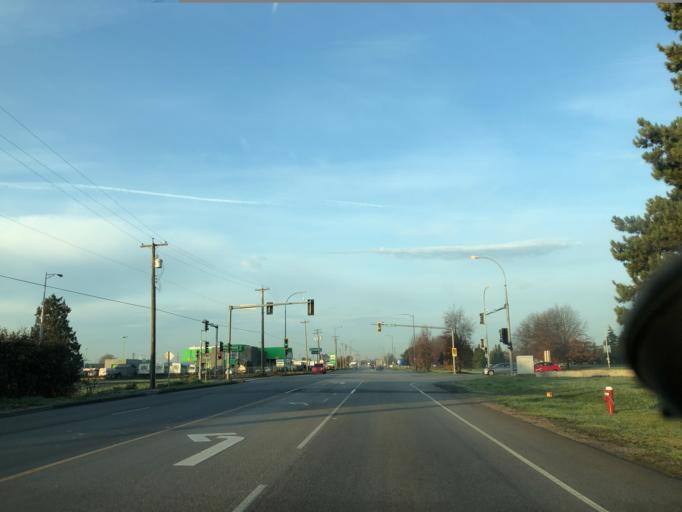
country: CA
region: British Columbia
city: Richmond
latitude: 49.1922
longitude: -123.1496
